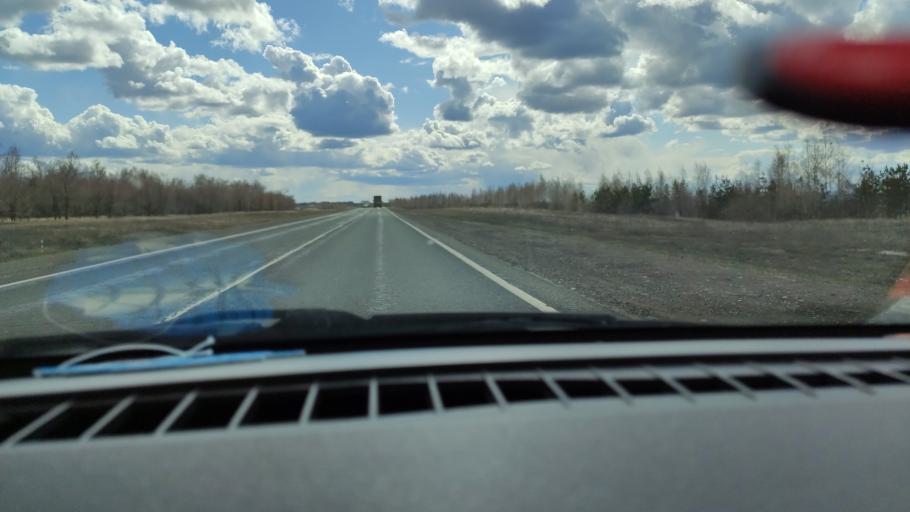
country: RU
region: Samara
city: Syzran'
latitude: 52.8569
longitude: 48.2609
